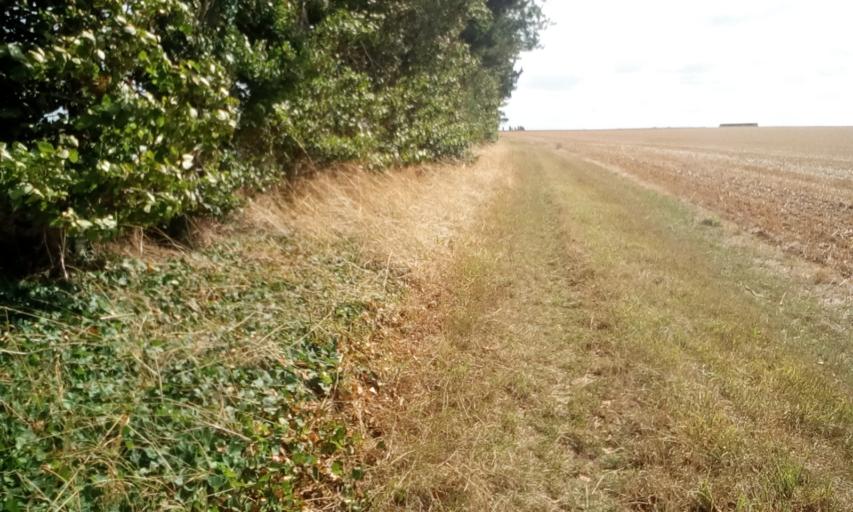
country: FR
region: Lower Normandy
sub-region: Departement du Calvados
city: Saint-Sylvain
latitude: 49.0823
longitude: -0.1979
